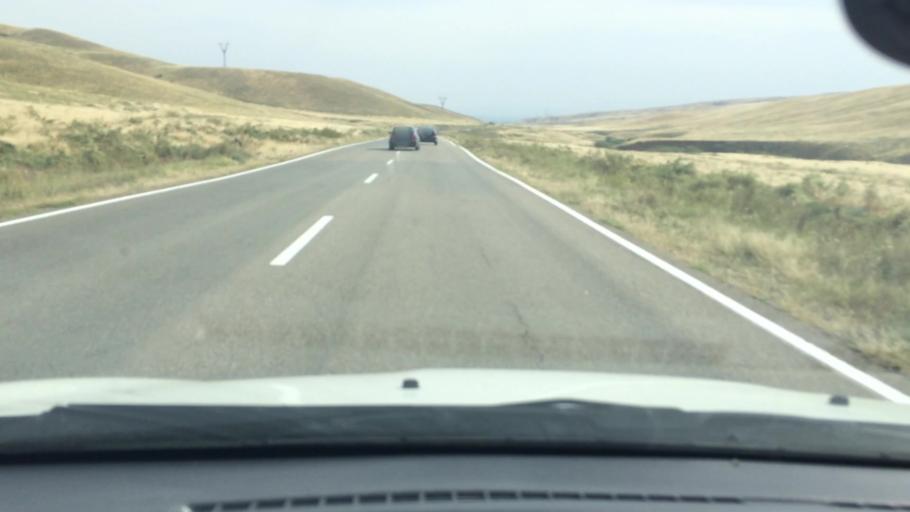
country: GE
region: Kvemo Kartli
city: Rust'avi
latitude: 41.5164
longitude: 44.9437
